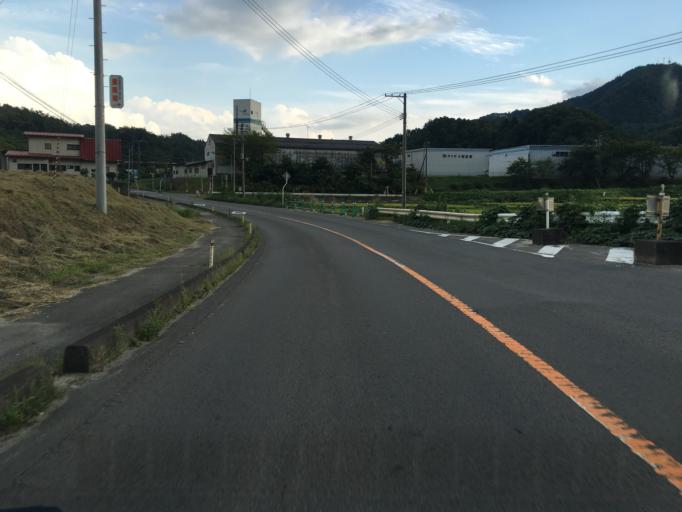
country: JP
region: Fukushima
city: Hobaramachi
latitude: 37.7666
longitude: 140.5953
